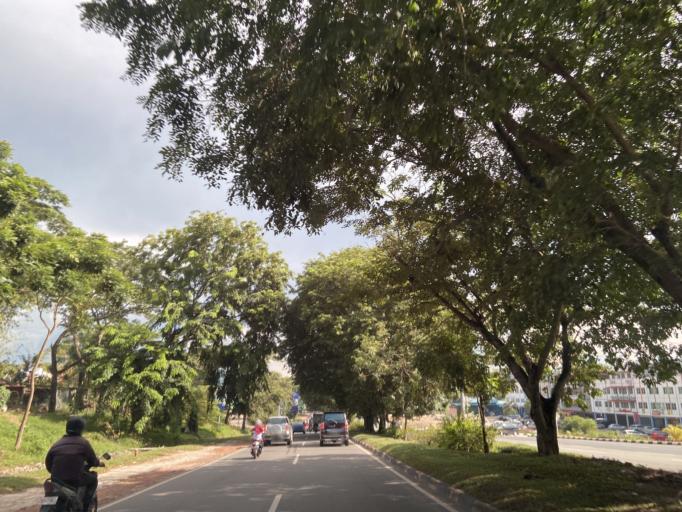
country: SG
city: Singapore
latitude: 1.1071
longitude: 104.0407
